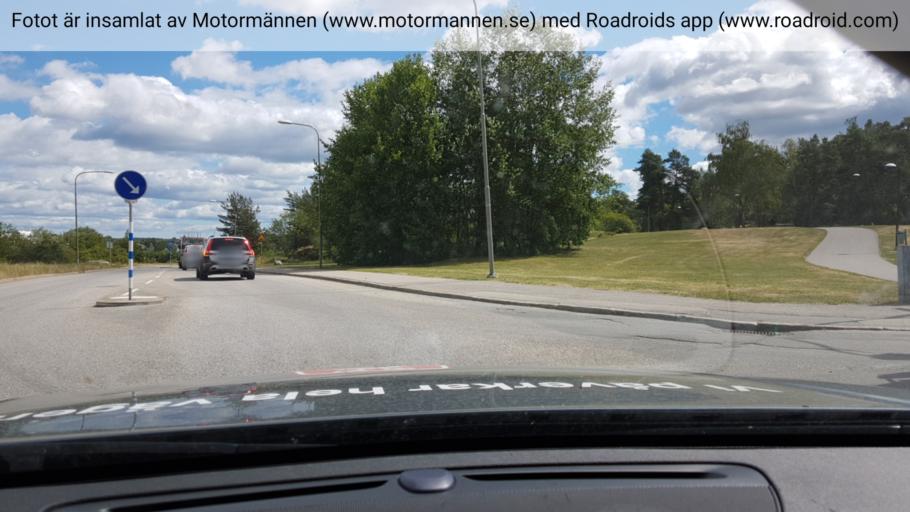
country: SE
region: Stockholm
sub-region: Stockholms Kommun
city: Arsta
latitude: 59.2889
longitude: 18.0386
